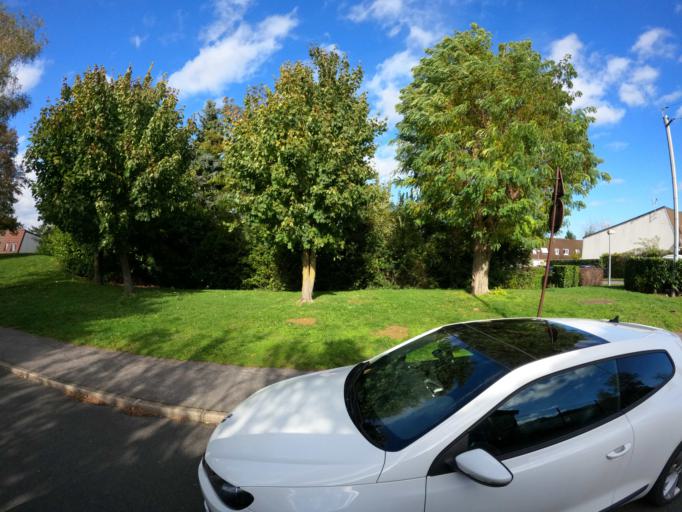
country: FR
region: Ile-de-France
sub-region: Departement de Seine-et-Marne
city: Esbly
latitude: 48.8942
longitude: 2.8125
